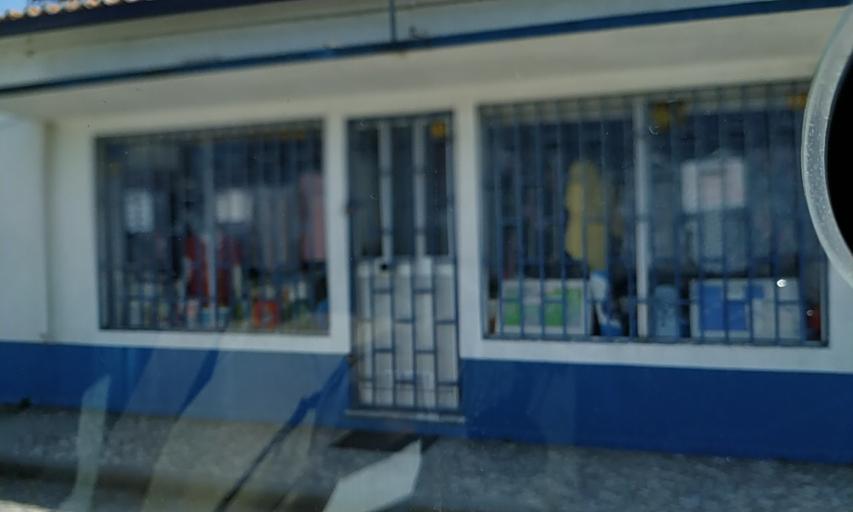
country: PT
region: Setubal
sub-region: Palmela
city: Palmela
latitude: 38.6076
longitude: -8.7766
